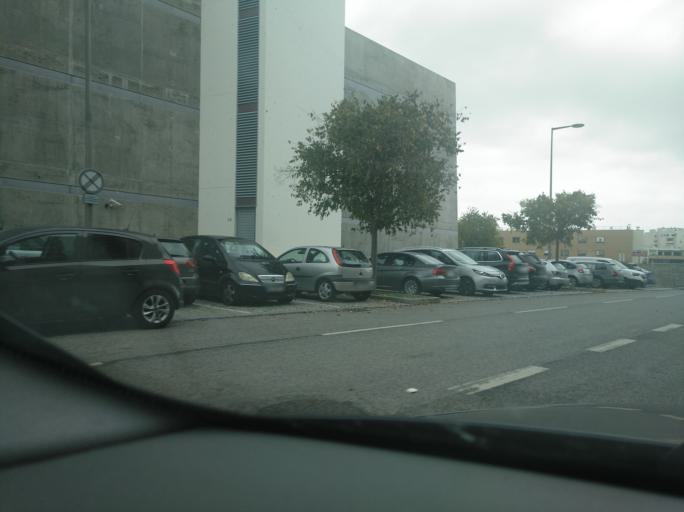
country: PT
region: Lisbon
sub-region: Odivelas
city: Pontinha
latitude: 38.7486
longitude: -9.1764
